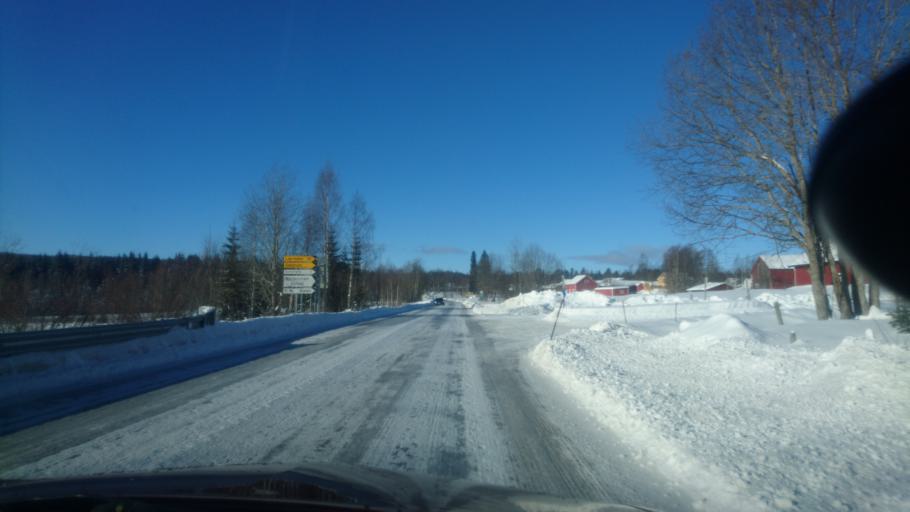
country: NO
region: Hedmark
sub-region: Trysil
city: Innbygda
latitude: 61.2528
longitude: 12.5339
